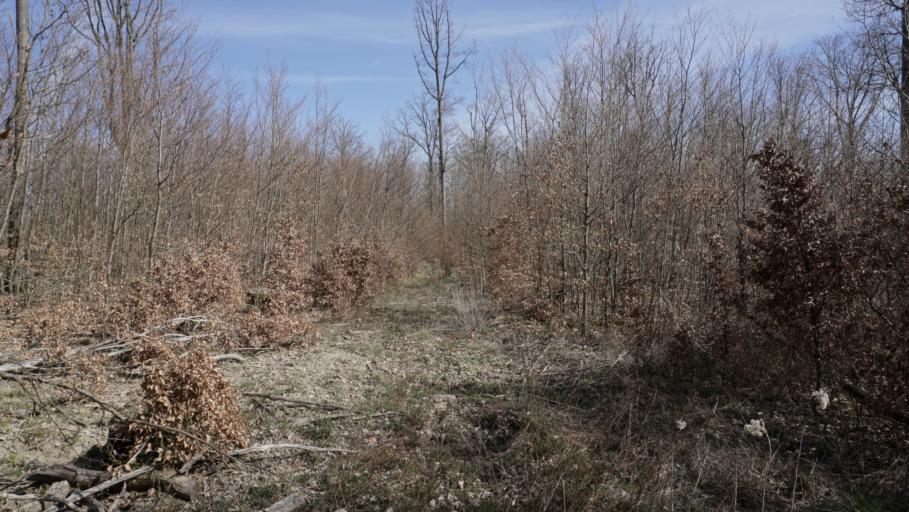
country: DE
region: Baden-Wuerttemberg
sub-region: Karlsruhe Region
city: Mosbach
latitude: 49.3808
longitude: 9.1441
